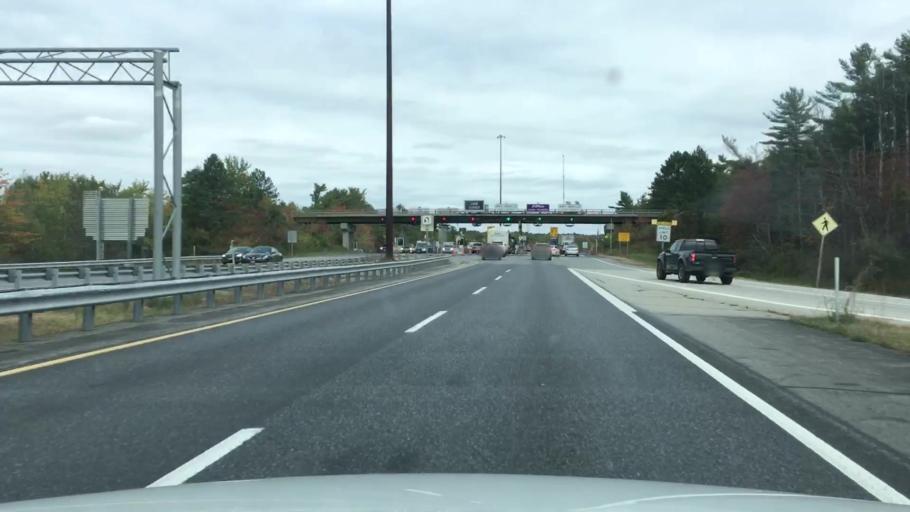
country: US
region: Maine
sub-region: Kennebec County
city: Gardiner
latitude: 44.2114
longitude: -69.8243
